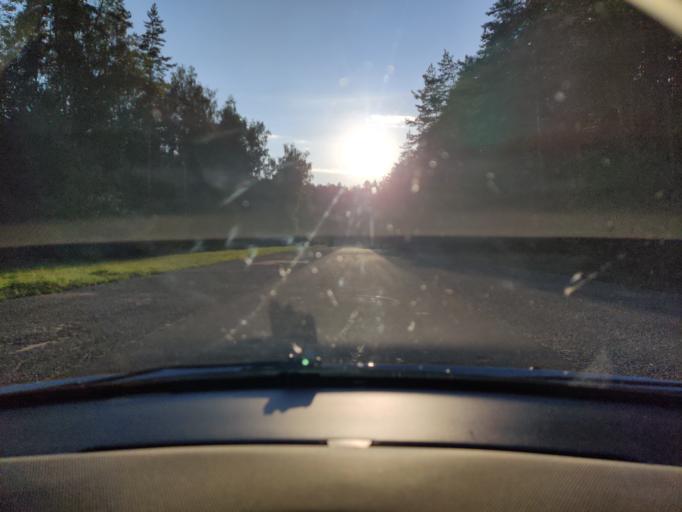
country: DE
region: Bavaria
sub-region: Upper Palatinate
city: Nabburg
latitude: 49.4575
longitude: 12.1626
